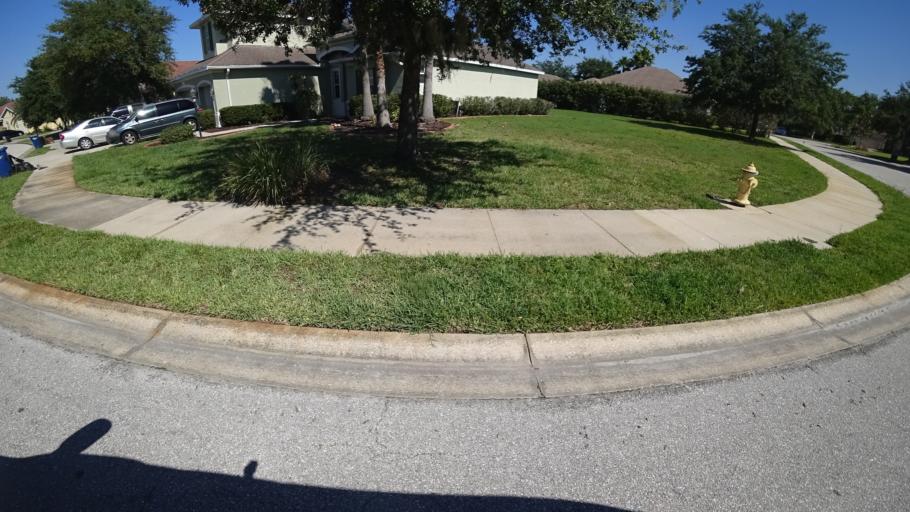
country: US
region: Florida
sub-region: Manatee County
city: Ellenton
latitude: 27.5674
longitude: -82.4382
